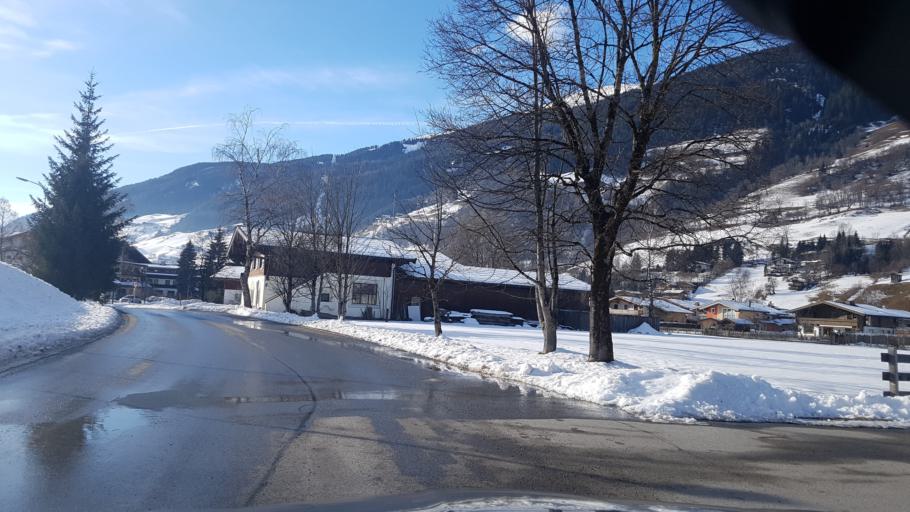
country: AT
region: Salzburg
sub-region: Politischer Bezirk Zell am See
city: Bramberg am Wildkogel
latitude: 47.2732
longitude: 12.3537
